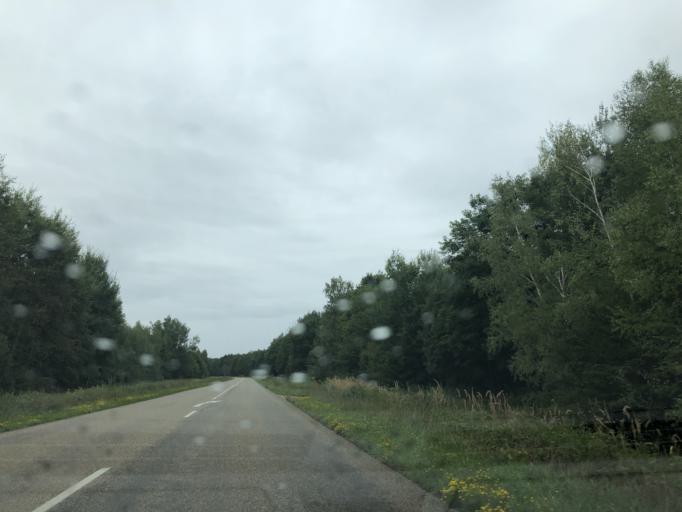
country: DE
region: Rheinland-Pfalz
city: Scheibenhardt
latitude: 48.9819
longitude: 8.1226
